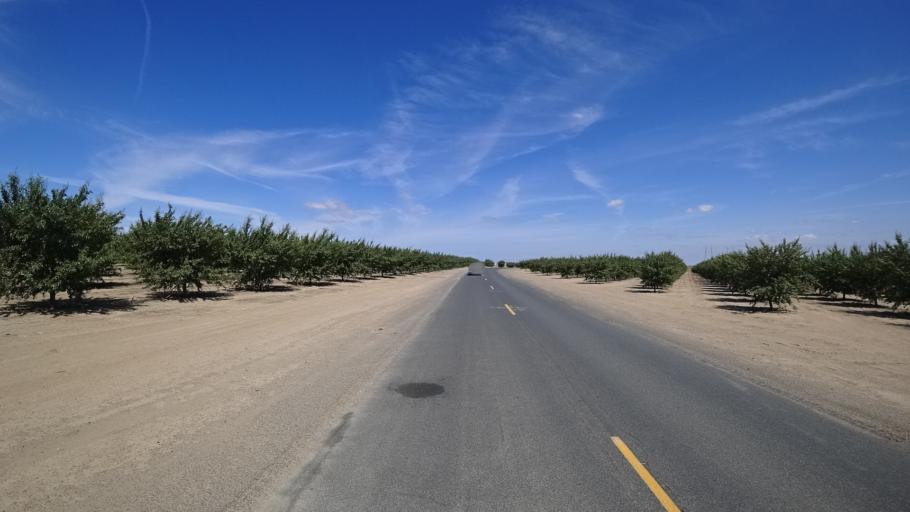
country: US
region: California
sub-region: Kings County
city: Kettleman City
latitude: 35.9826
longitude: -119.9511
